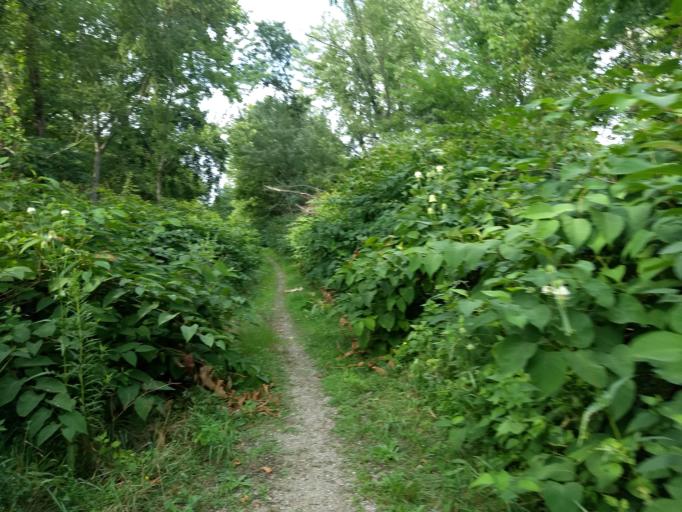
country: US
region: Pennsylvania
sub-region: Armstrong County
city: Freeport
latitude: 40.6721
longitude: -79.6930
